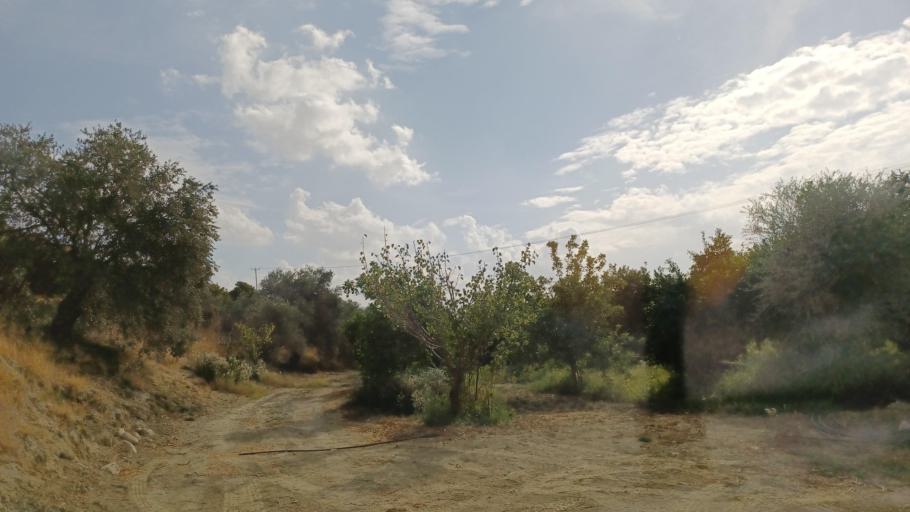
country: CY
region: Pafos
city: Polis
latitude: 35.0301
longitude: 32.4381
